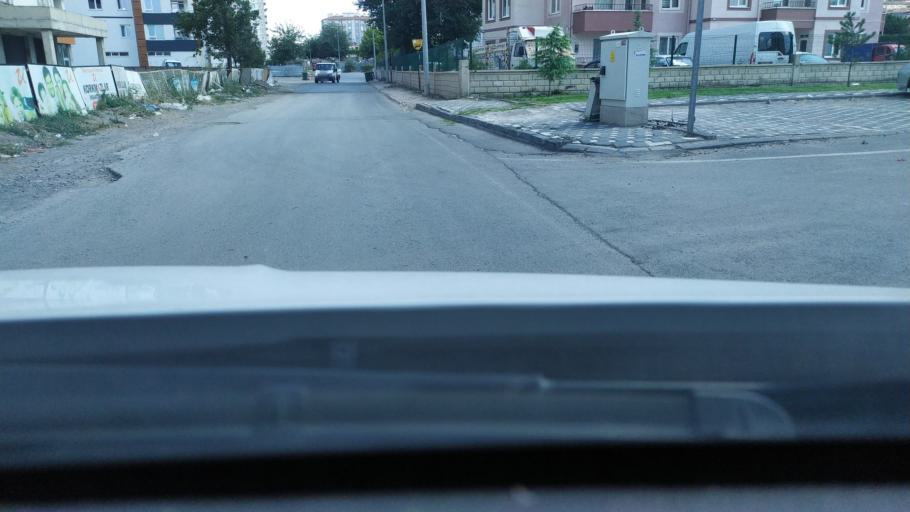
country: TR
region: Kayseri
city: Kayseri
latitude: 38.7103
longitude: 35.4728
